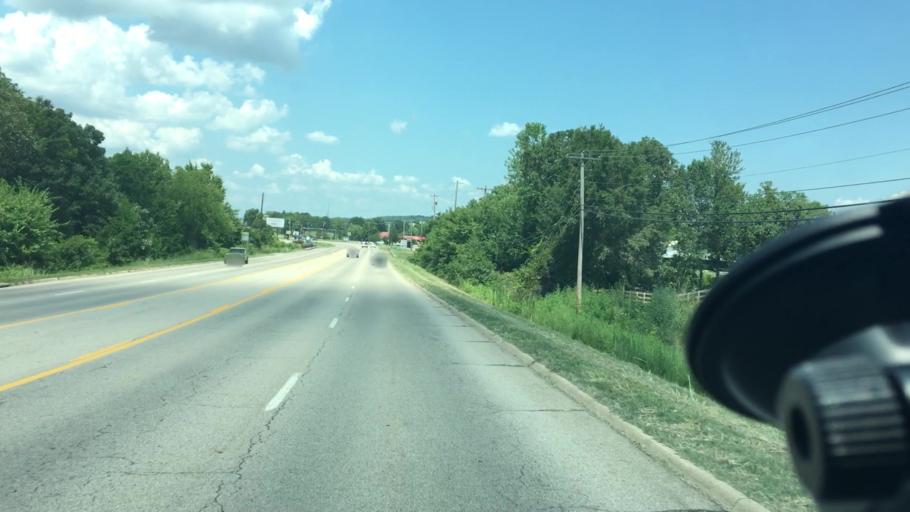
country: US
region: Arkansas
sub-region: Sebastian County
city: Barling
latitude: 35.3416
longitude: -94.3224
